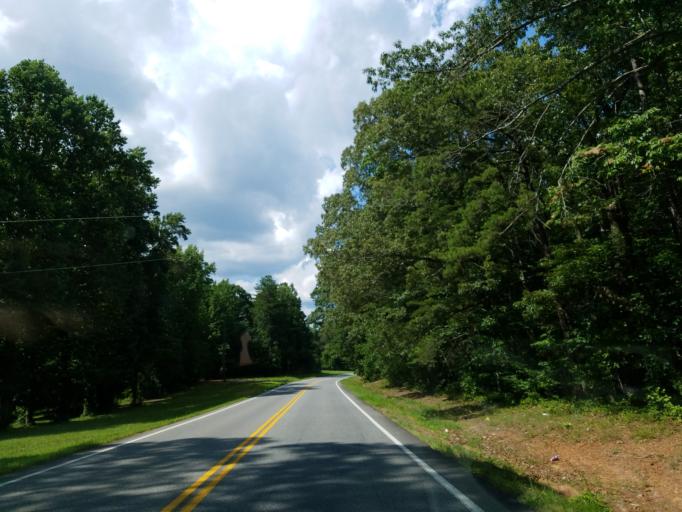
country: US
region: Georgia
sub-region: Dawson County
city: Dawsonville
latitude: 34.4459
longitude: -84.0902
